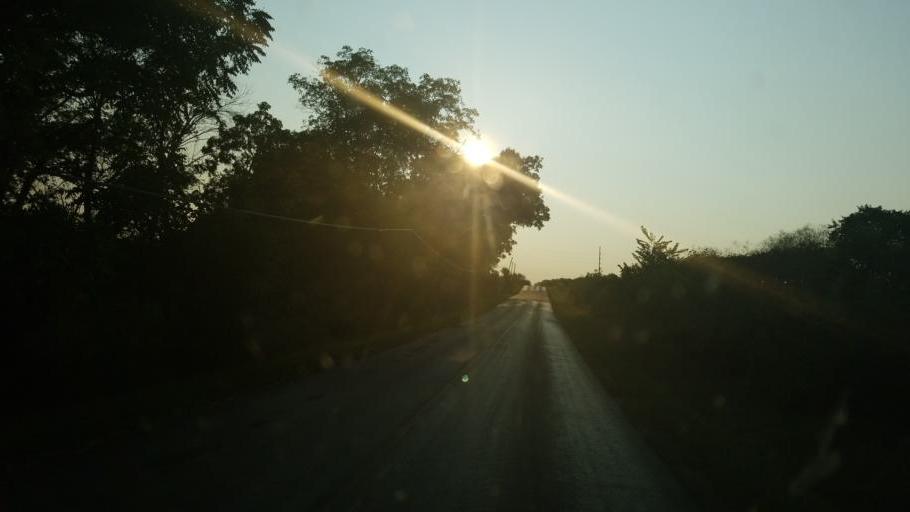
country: US
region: Ohio
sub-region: Wayne County
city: Shreve
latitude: 40.6682
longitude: -82.0303
